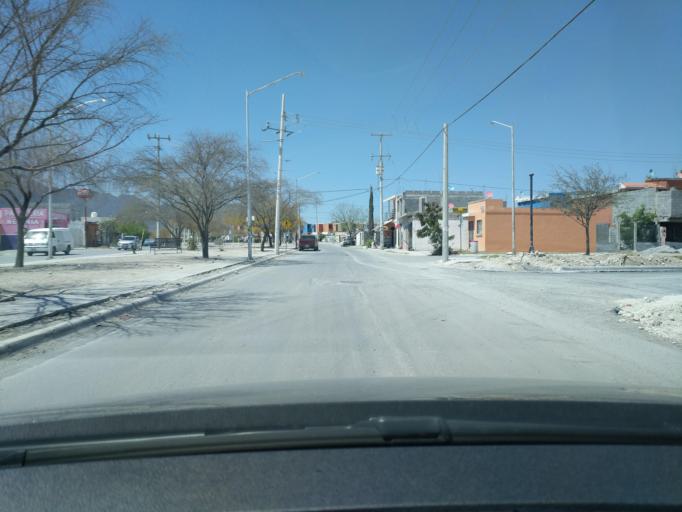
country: MX
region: Nuevo Leon
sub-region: Salinas Victoria
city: Las Torres
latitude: 25.9640
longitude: -100.3056
